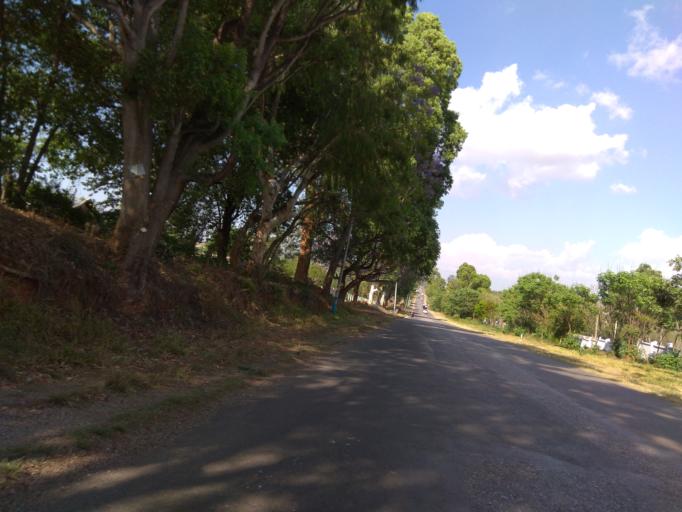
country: MM
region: Shan
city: Taunggyi
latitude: 20.6666
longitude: 96.6513
